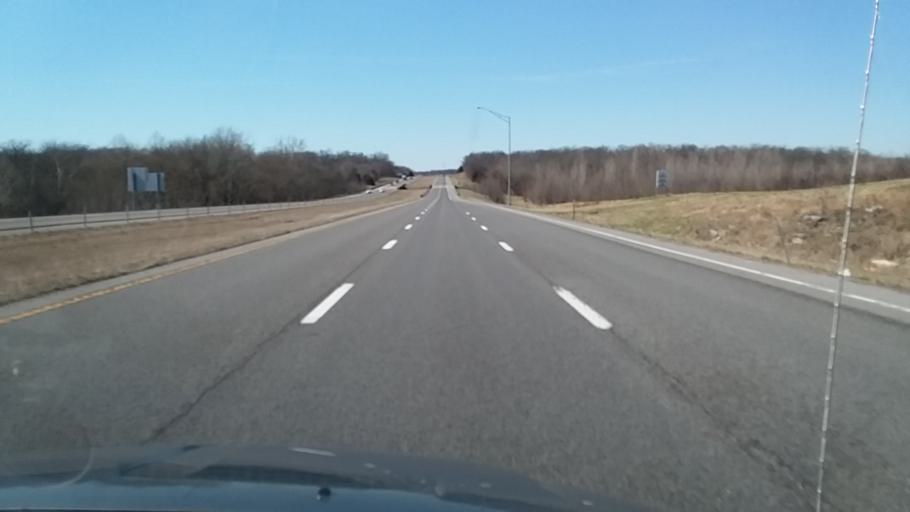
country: US
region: Missouri
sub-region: Perry County
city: Perryville
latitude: 37.5799
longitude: -89.7618
